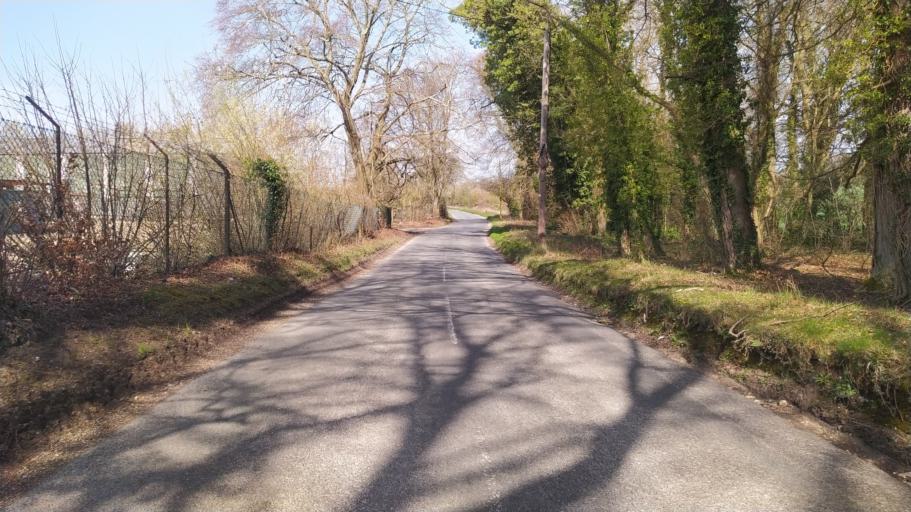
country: GB
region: England
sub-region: Hampshire
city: Four Marks
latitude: 51.0660
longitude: -1.1088
